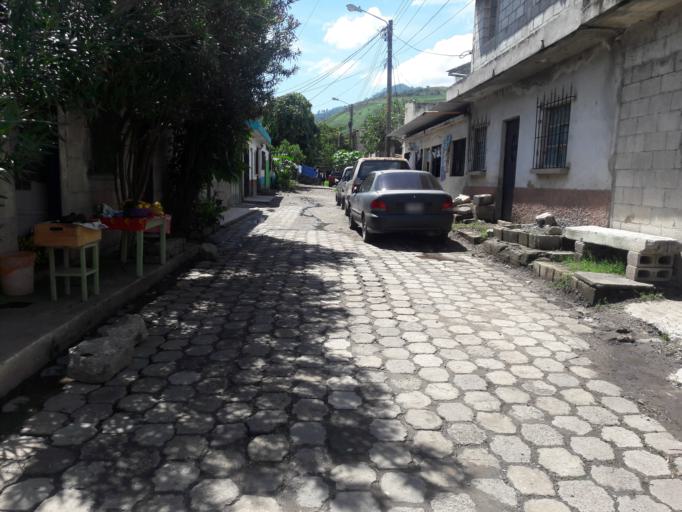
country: GT
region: Guatemala
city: Amatitlan
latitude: 14.4636
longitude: -90.5783
